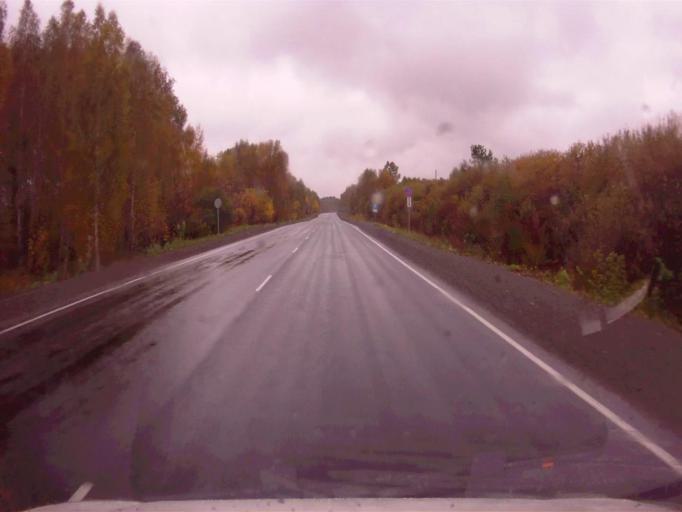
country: RU
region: Chelyabinsk
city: Argayash
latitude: 55.4786
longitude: 60.7810
